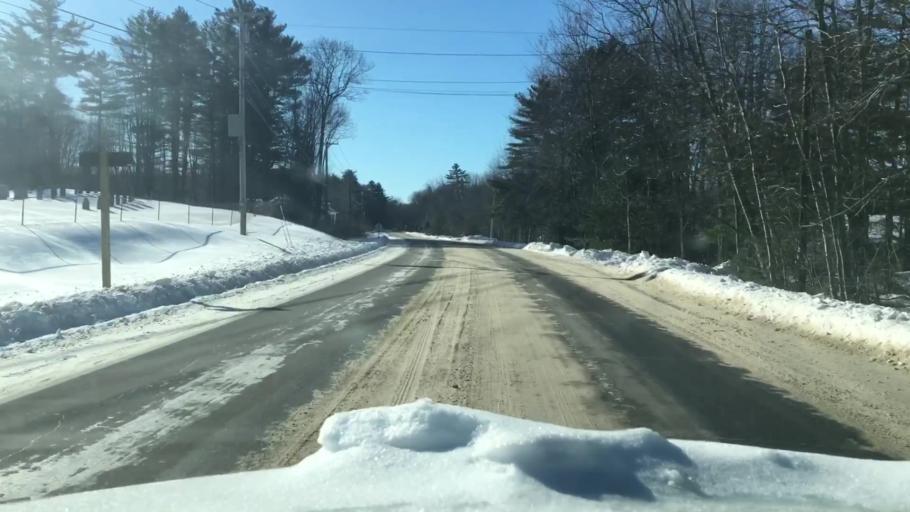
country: US
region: Maine
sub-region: Cumberland County
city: Brunswick
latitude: 43.9462
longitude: -69.9283
